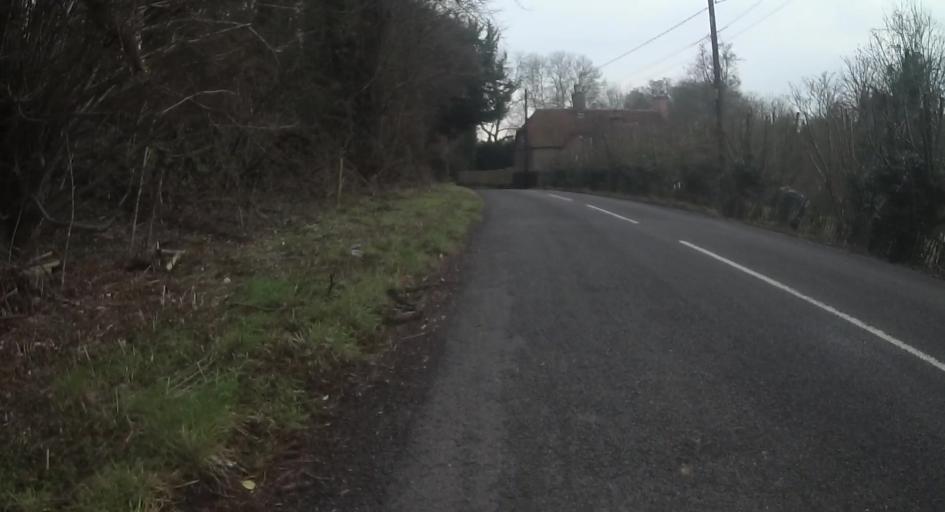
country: GB
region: England
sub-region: Hampshire
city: Highclere
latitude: 51.2306
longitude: -1.3813
